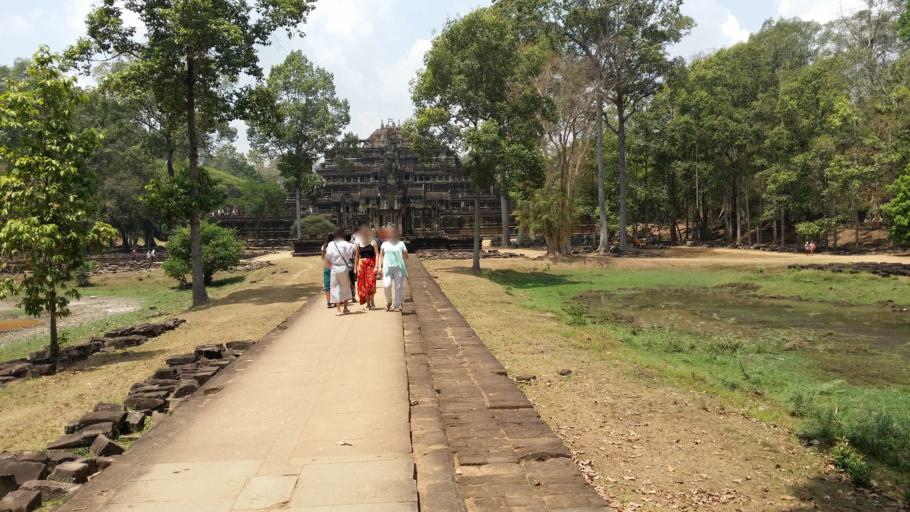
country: KH
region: Siem Reap
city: Siem Reap
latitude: 13.4438
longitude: 103.8585
